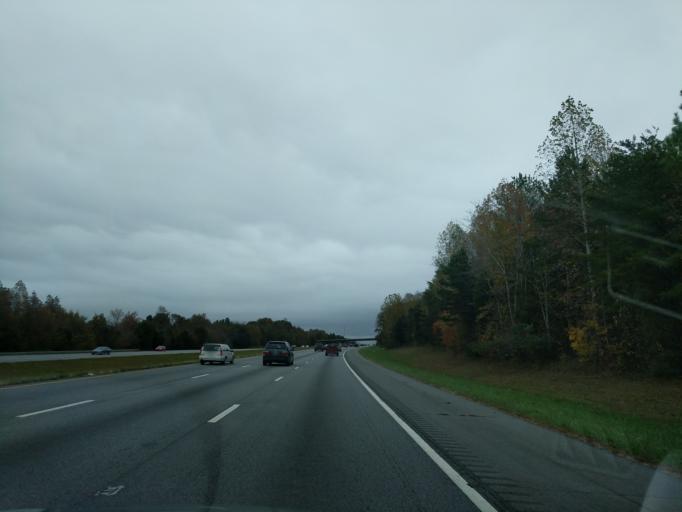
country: US
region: North Carolina
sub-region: Randolph County
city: Trinity
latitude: 35.8832
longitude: -79.9966
